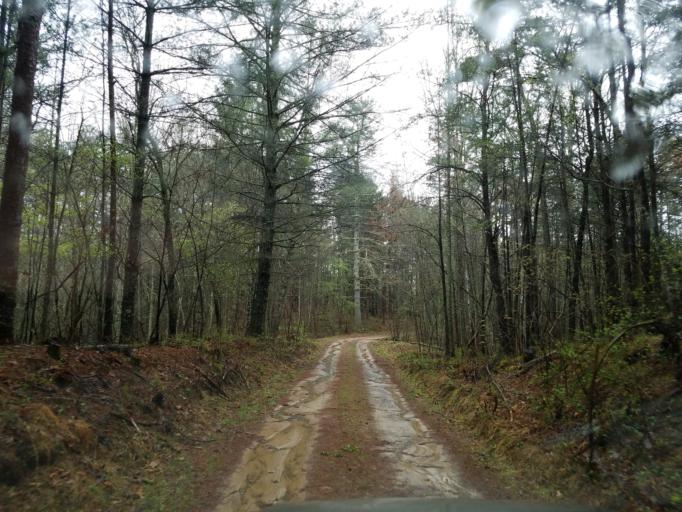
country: US
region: Georgia
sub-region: Fannin County
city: Blue Ridge
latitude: 34.8272
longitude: -84.2388
